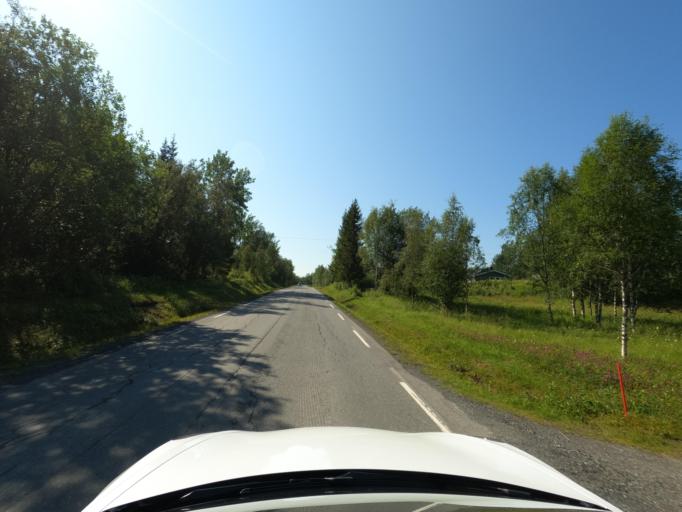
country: NO
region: Nordland
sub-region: Ballangen
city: Ballangen
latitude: 68.3596
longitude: 16.8764
